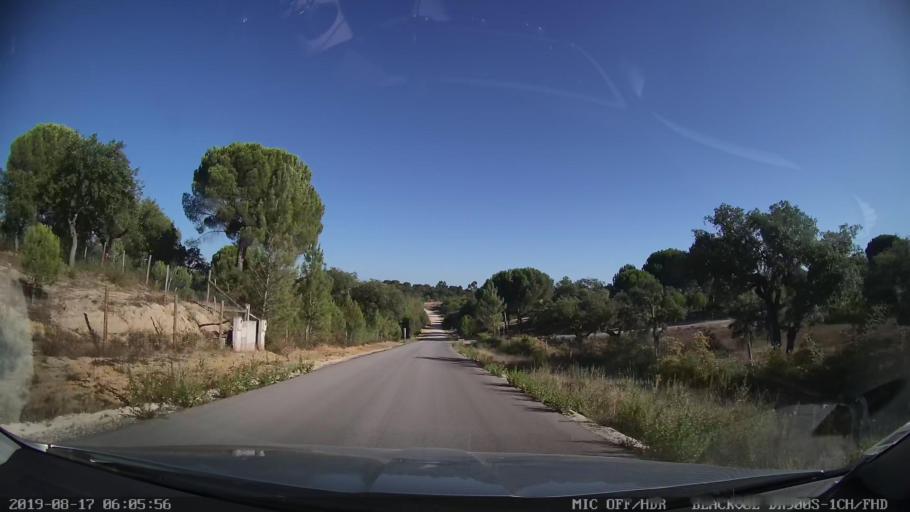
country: PT
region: Santarem
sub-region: Benavente
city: Poceirao
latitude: 38.8466
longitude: -8.6942
